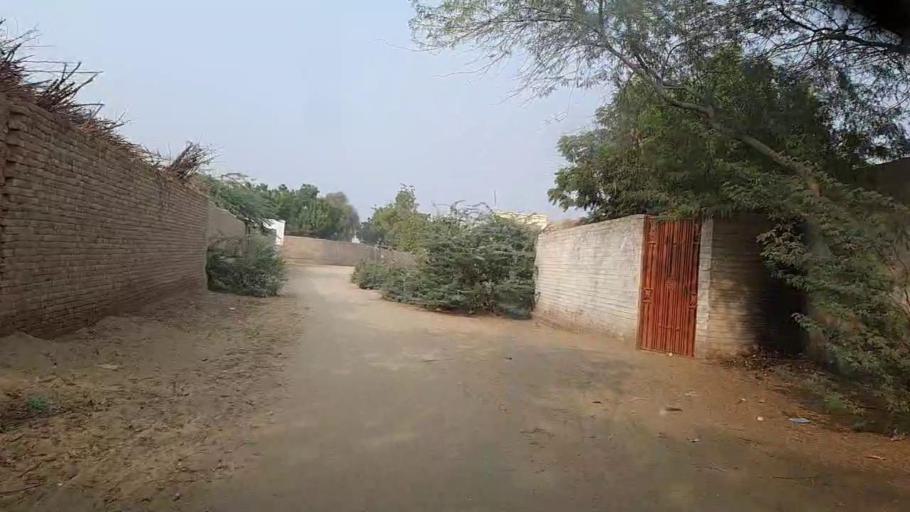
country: PK
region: Sindh
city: Bozdar
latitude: 27.1514
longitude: 68.6737
